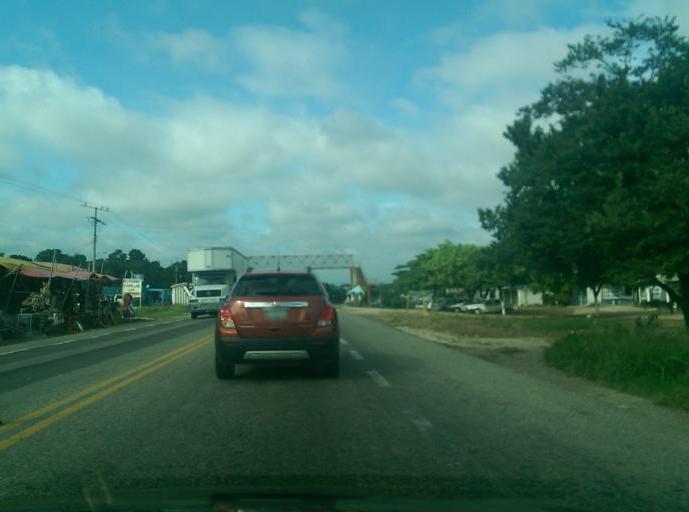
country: MX
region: Tabasco
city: Aquiles Serdan
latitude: 17.6993
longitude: -92.2588
